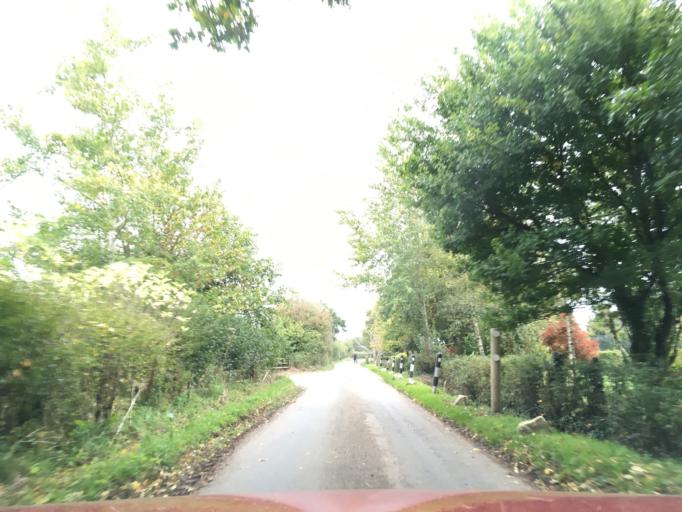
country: GB
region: England
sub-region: South Gloucestershire
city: Wickwar
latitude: 51.5991
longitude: -2.4348
